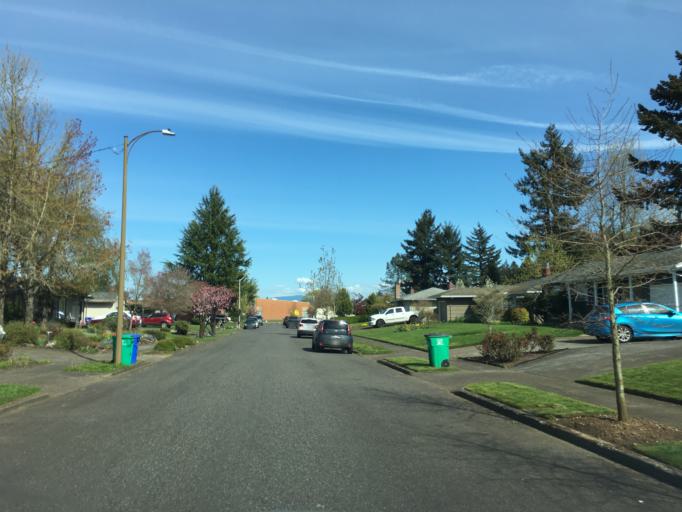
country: US
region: Oregon
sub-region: Multnomah County
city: Lents
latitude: 45.5420
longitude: -122.5346
